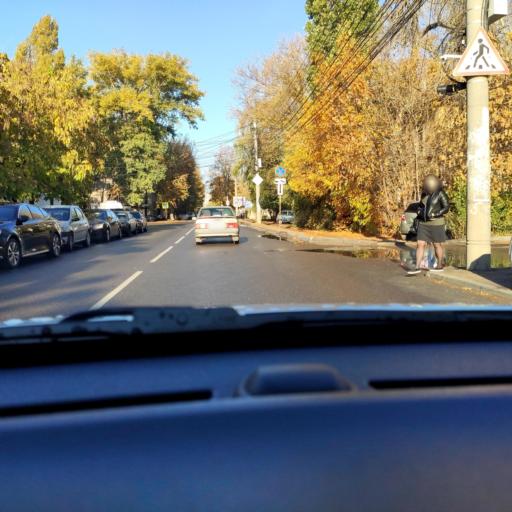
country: RU
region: Voronezj
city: Voronezh
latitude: 51.6850
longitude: 39.1811
